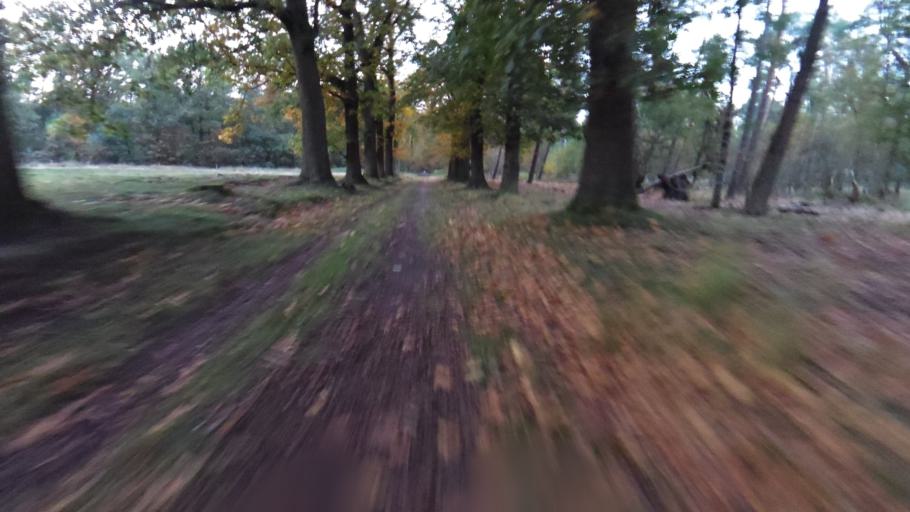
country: NL
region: Gelderland
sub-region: Gemeente Renkum
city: Oosterbeek
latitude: 52.0183
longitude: 5.8373
